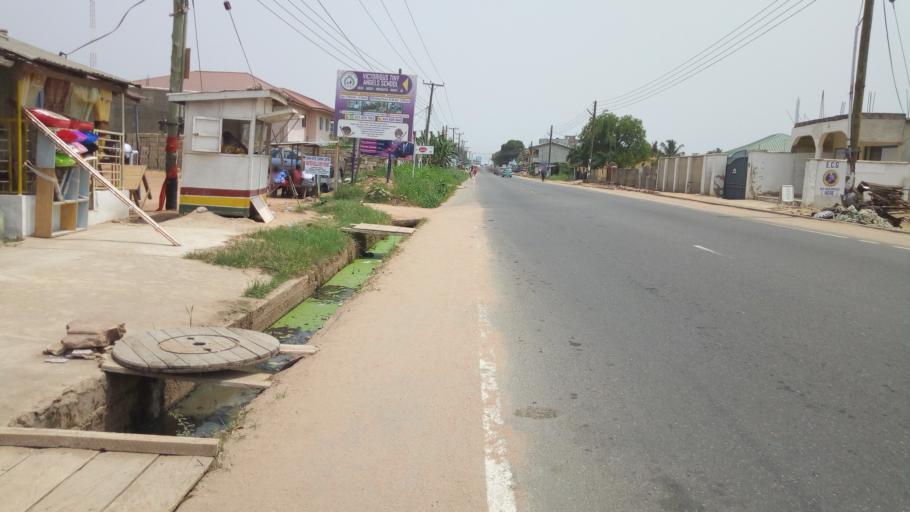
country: GH
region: Greater Accra
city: Gbawe
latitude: 5.5579
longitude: -0.3078
